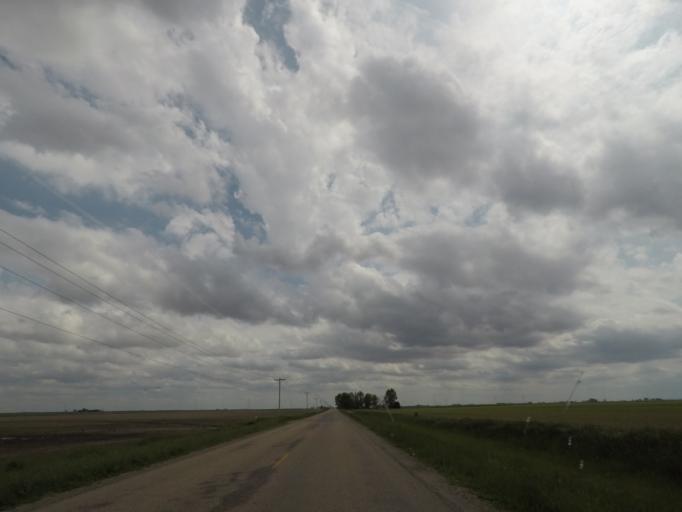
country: US
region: Illinois
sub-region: De Witt County
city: Clinton
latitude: 40.0902
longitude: -89.0859
